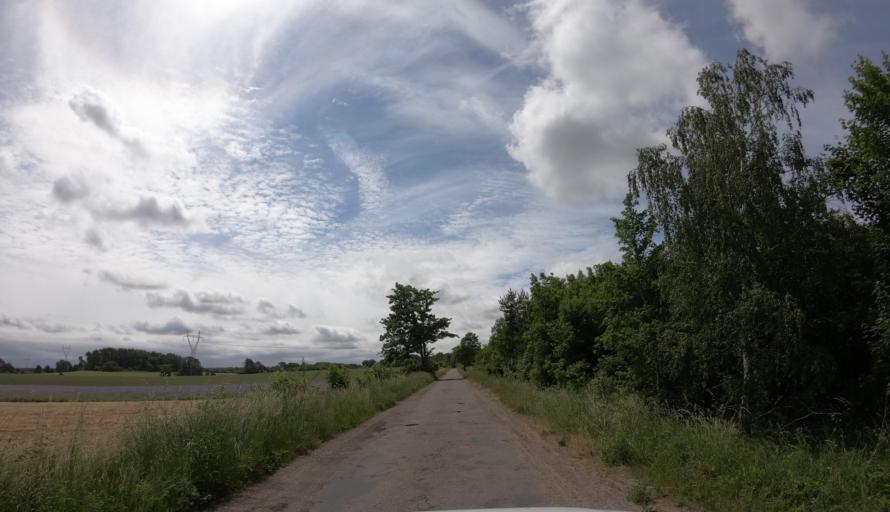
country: PL
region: West Pomeranian Voivodeship
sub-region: Powiat kamienski
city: Wolin
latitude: 53.8329
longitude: 14.7104
